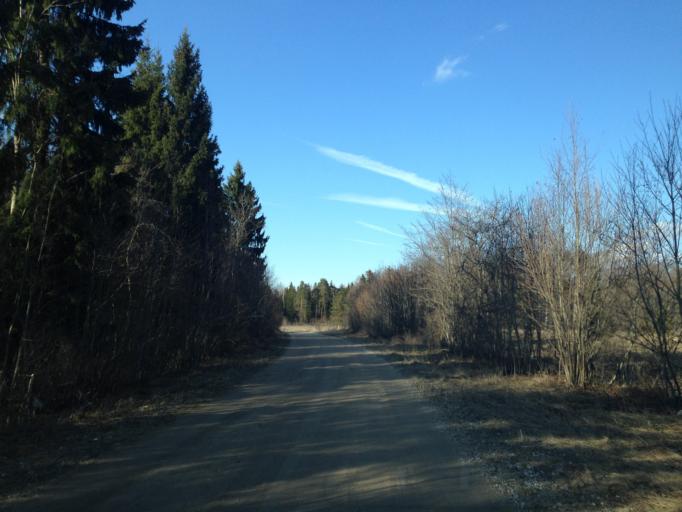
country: EE
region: Harju
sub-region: Nissi vald
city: Turba
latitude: 59.1163
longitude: 24.1609
